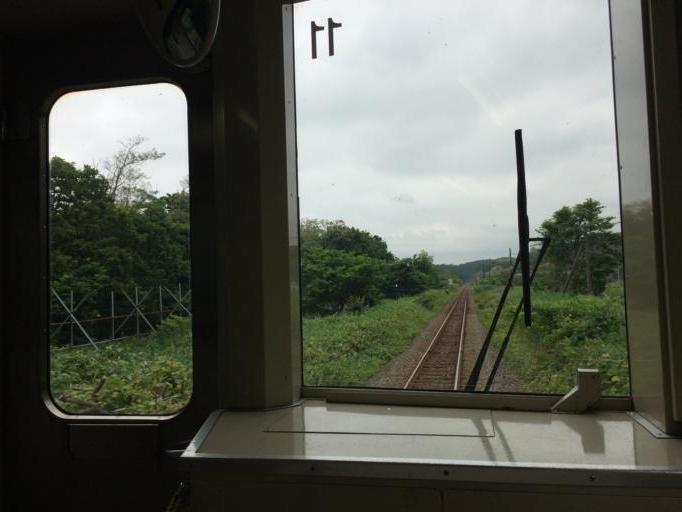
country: JP
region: Hokkaido
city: Yoichi
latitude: 43.1928
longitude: 140.8270
